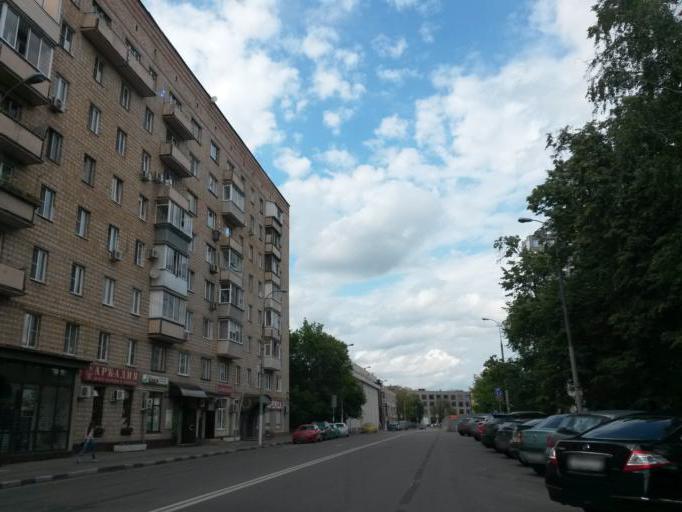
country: RU
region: Moskovskaya
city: Kozhukhovo
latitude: 55.7065
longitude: 37.6553
